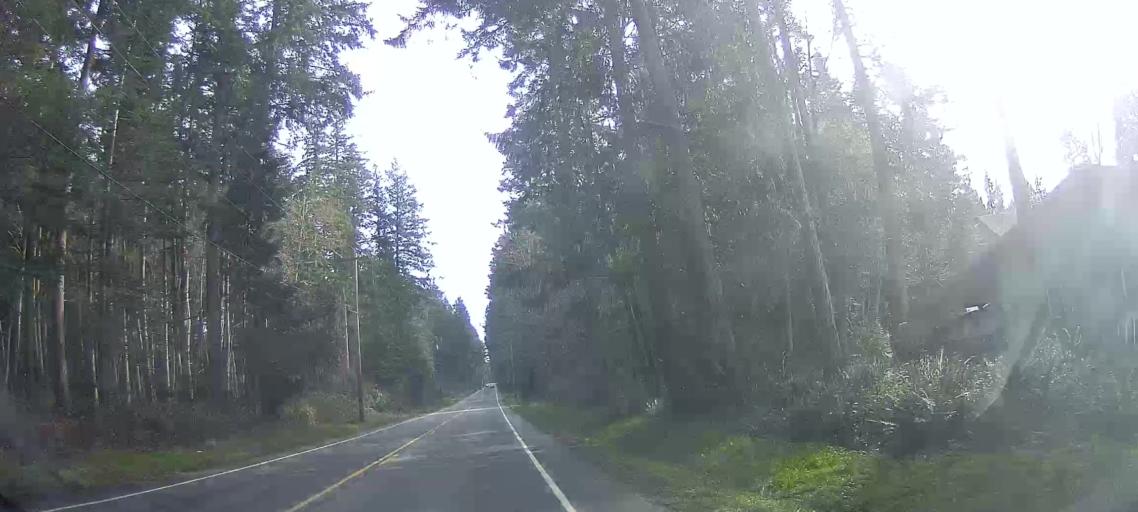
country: US
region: Washington
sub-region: Island County
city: Camano
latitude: 48.1285
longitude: -122.4607
